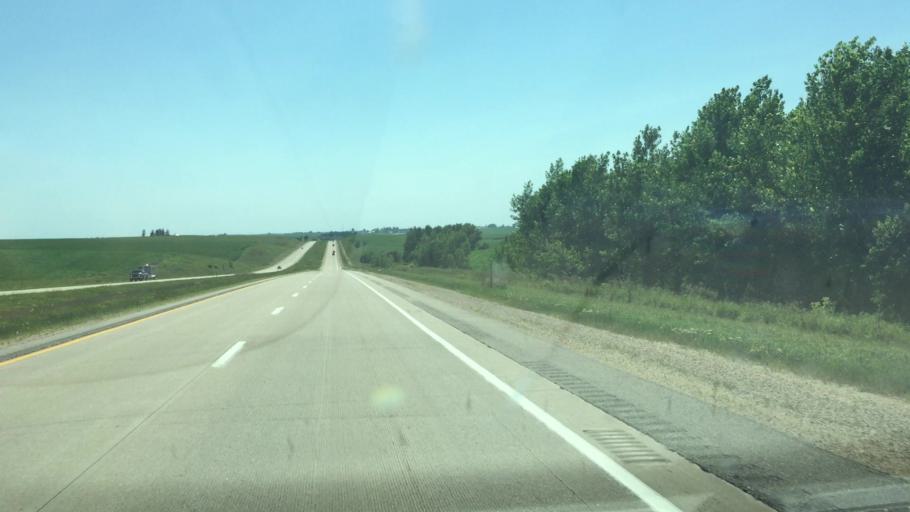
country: US
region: Iowa
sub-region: Dubuque County
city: Peosta
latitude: 42.3622
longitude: -90.8052
